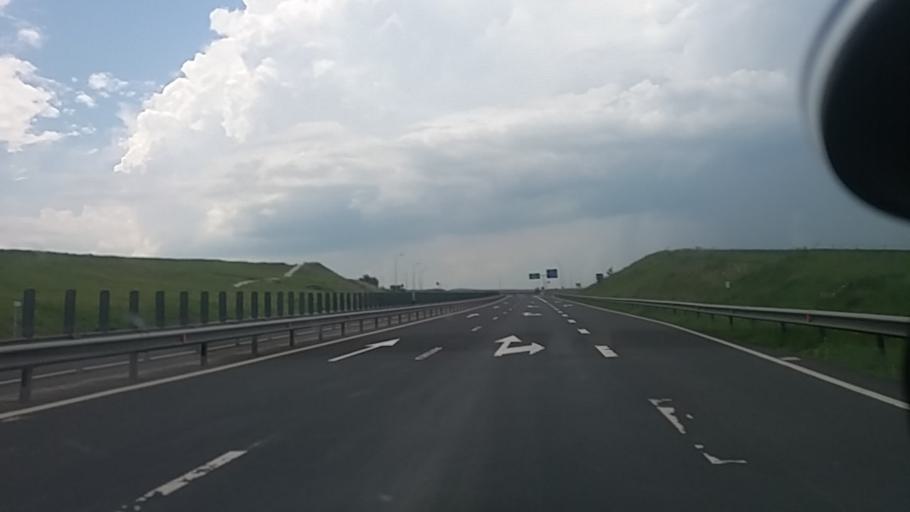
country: RO
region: Alba
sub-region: Comuna Garbova
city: Garbova
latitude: 45.9165
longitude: 23.7278
